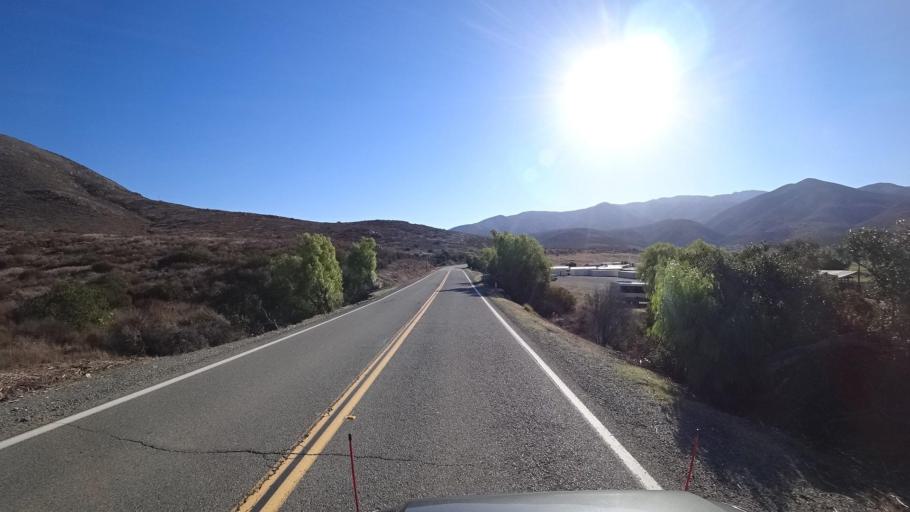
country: US
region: California
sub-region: San Diego County
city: Jamul
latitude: 32.6359
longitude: -116.8923
